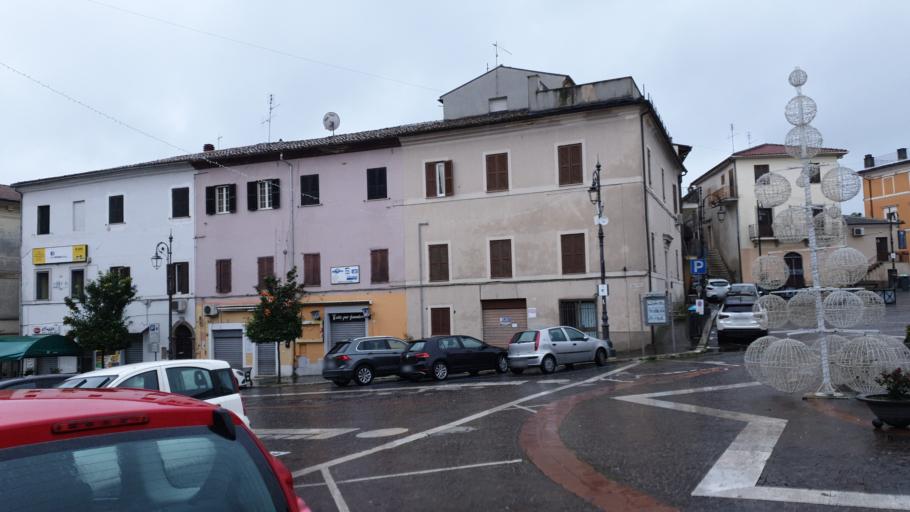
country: IT
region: Latium
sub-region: Provincia di Frosinone
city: Ceccano
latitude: 41.5696
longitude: 13.3329
